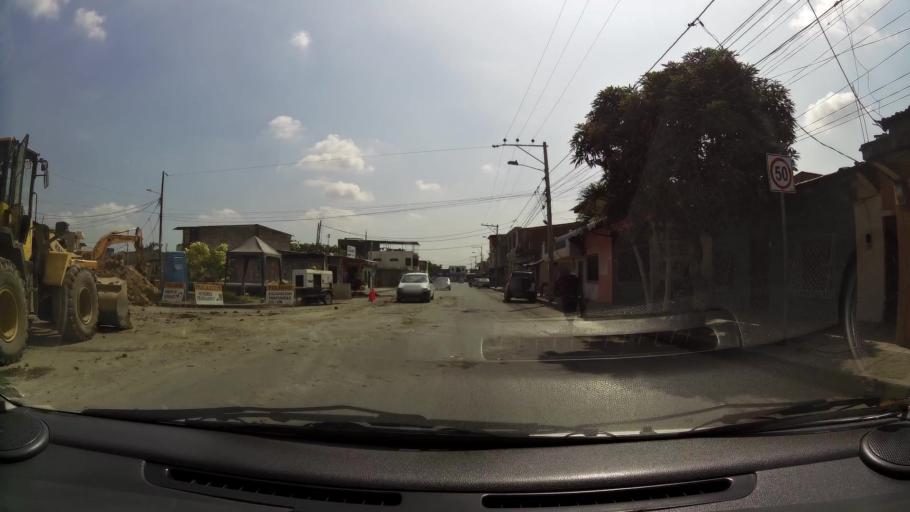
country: EC
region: Guayas
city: Eloy Alfaro
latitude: -2.1507
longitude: -79.8324
